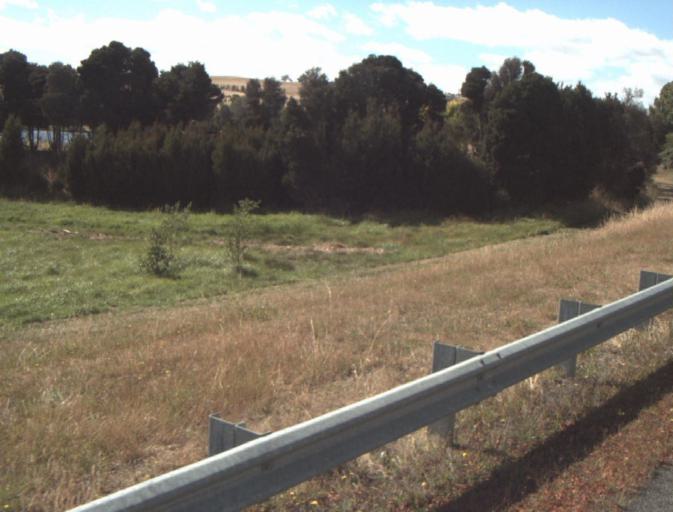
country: AU
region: Tasmania
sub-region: Launceston
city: Newstead
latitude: -41.4302
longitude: 147.1872
